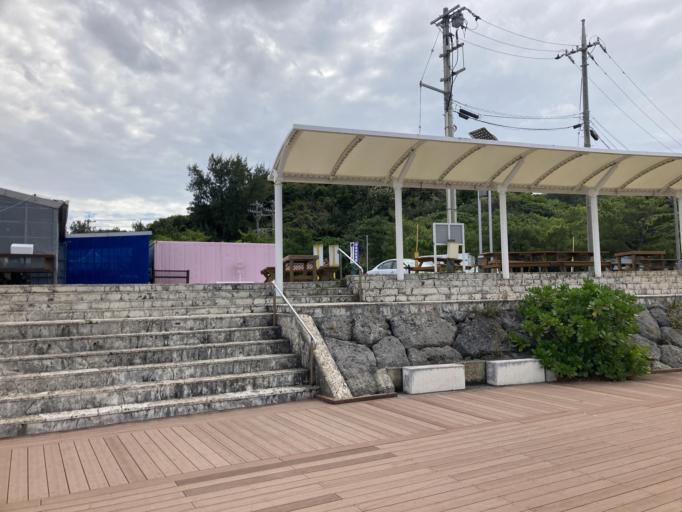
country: JP
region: Okinawa
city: Ishikawa
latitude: 26.4361
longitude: 127.7943
